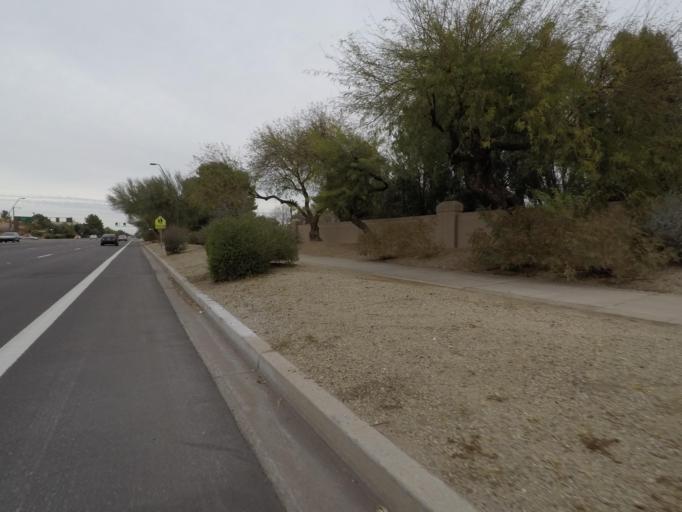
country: US
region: Arizona
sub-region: Maricopa County
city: Guadalupe
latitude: 33.3406
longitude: -111.9283
